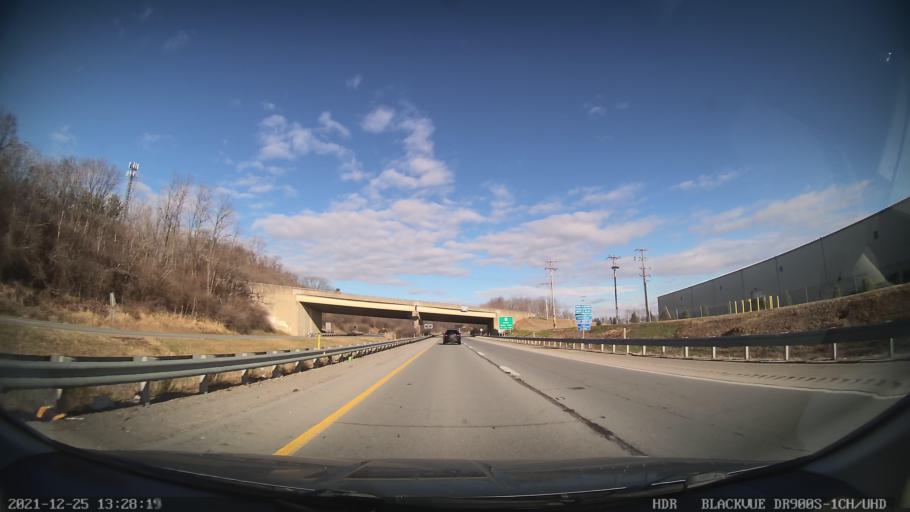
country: US
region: Pennsylvania
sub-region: York County
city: Shiloh
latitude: 39.9467
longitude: -76.7968
